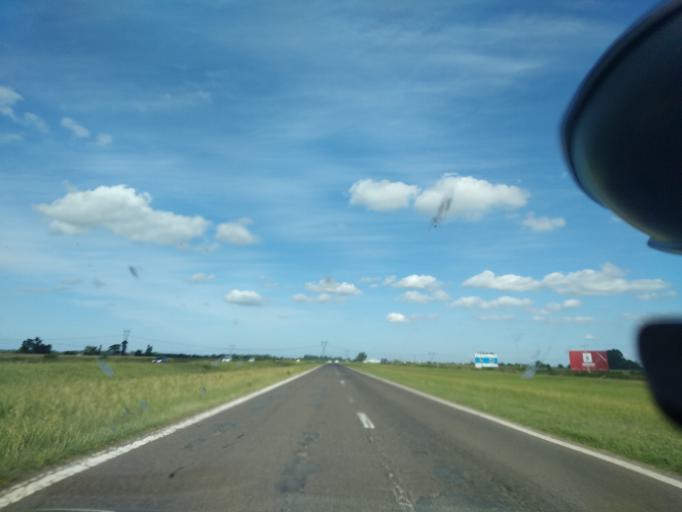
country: AR
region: Santa Fe
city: Roldan
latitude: -32.9194
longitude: -60.9292
